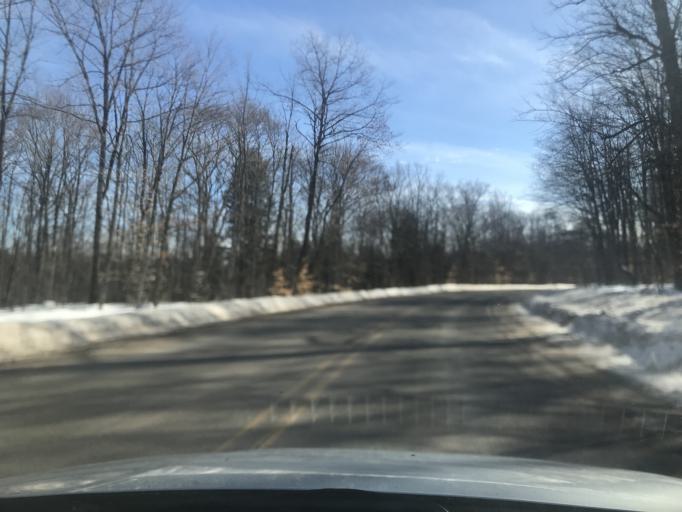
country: US
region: Michigan
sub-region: Dickinson County
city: Kingsford
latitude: 45.4181
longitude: -88.3974
